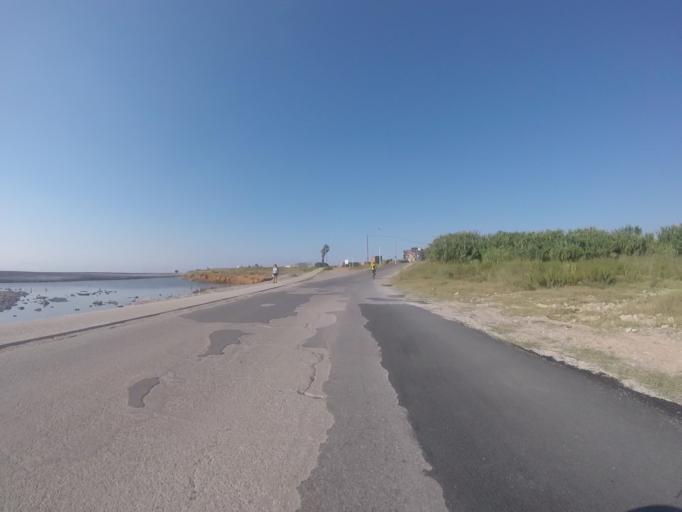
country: ES
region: Valencia
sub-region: Provincia de Castello
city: Benicarlo
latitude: 40.4195
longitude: 0.4365
